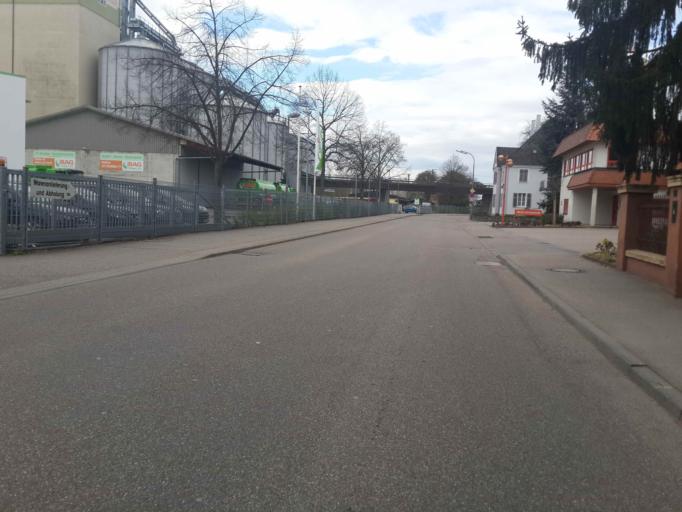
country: DE
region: Baden-Wuerttemberg
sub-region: Regierungsbezirk Stuttgart
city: Untereisesheim
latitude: 49.2284
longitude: 9.2083
